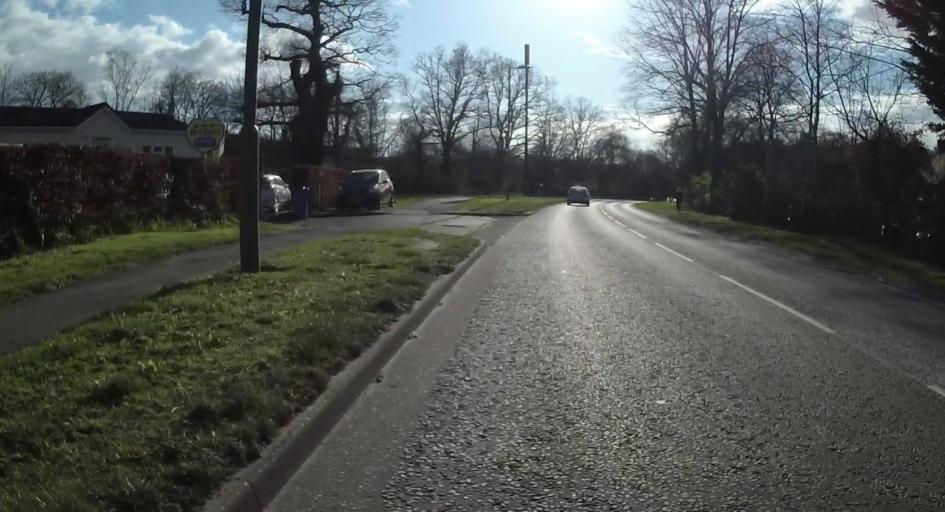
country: GB
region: England
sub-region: Hampshire
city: Farnborough
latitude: 51.2941
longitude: -0.7939
